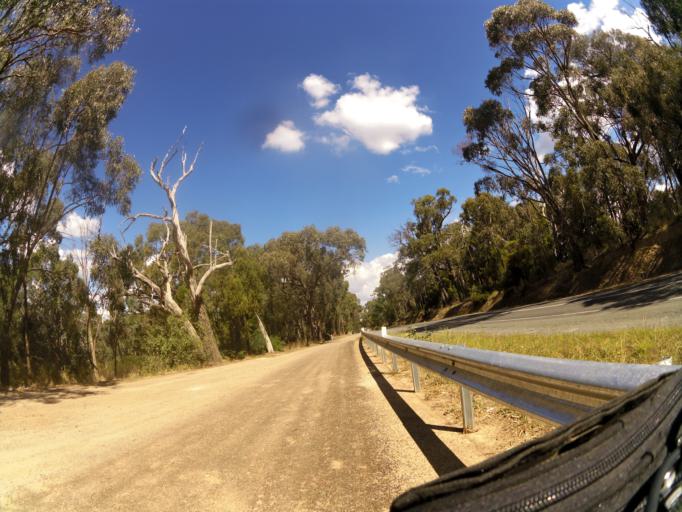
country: AU
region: Victoria
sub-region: Mansfield
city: Mansfield
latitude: -36.8402
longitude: 146.0074
